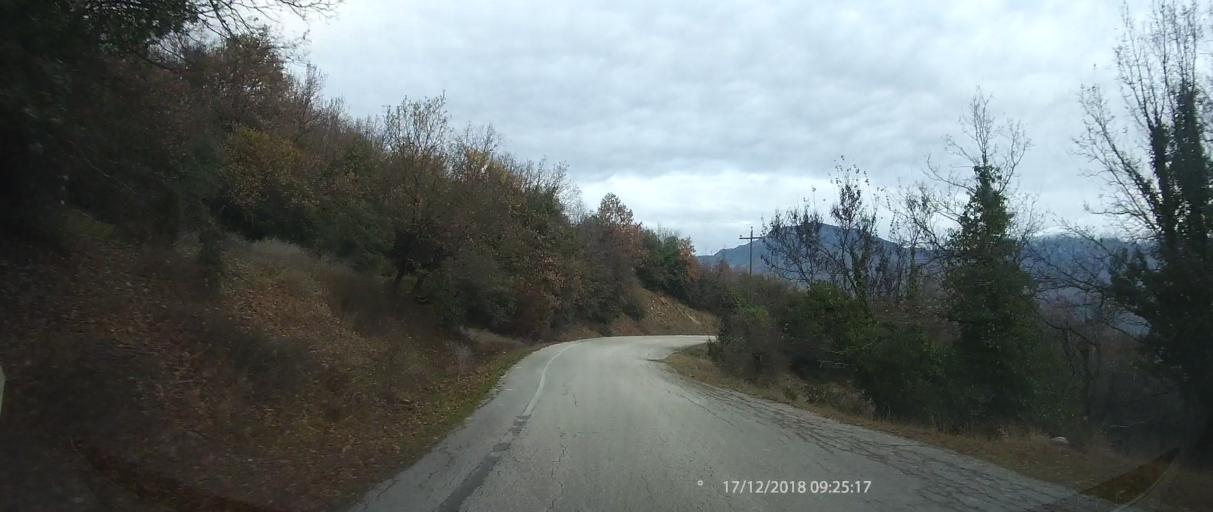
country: GR
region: Epirus
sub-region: Nomos Ioanninon
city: Kalpaki
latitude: 39.9376
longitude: 20.6714
